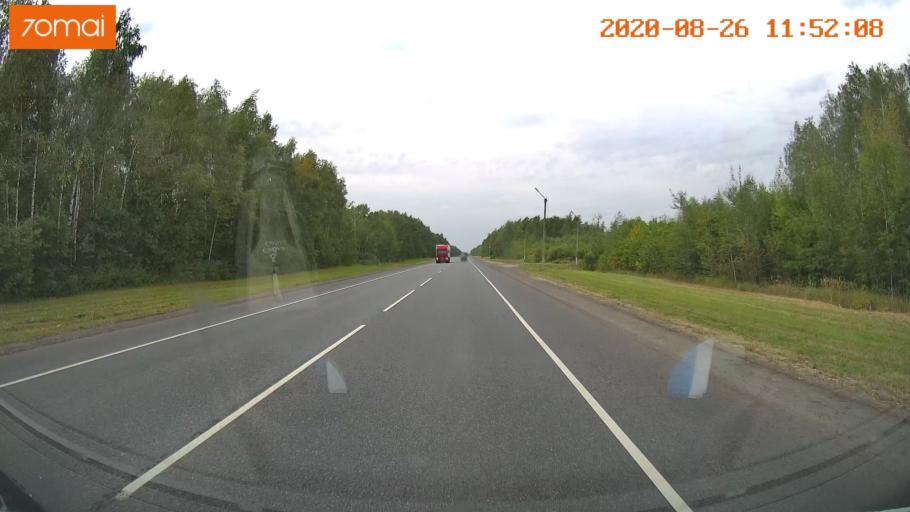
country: RU
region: Rjazan
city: Lesnoy
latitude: 54.2952
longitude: 40.4627
